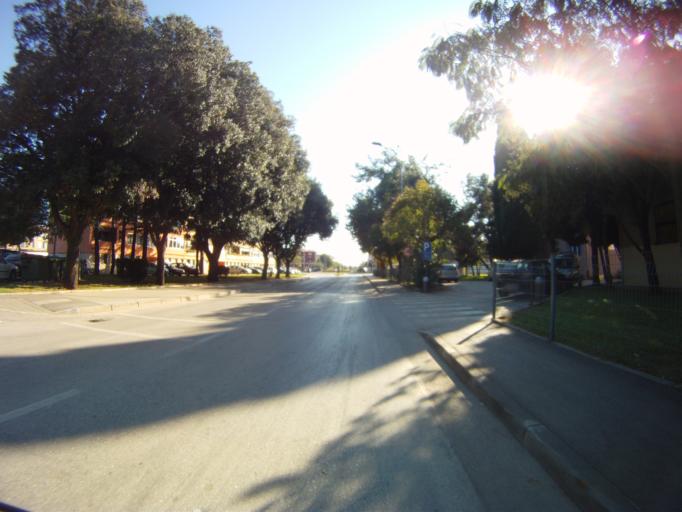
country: HR
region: Istarska
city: Umag
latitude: 45.4321
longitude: 13.5238
